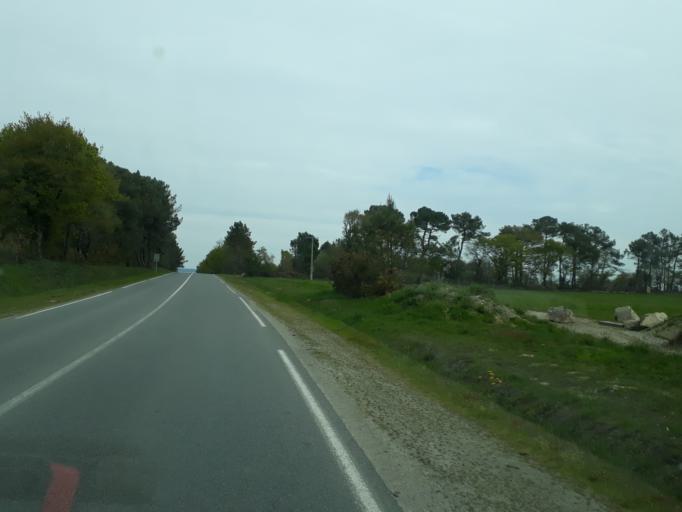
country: FR
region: Brittany
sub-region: Departement du Morbihan
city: Surzur
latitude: 47.5933
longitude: -2.6237
